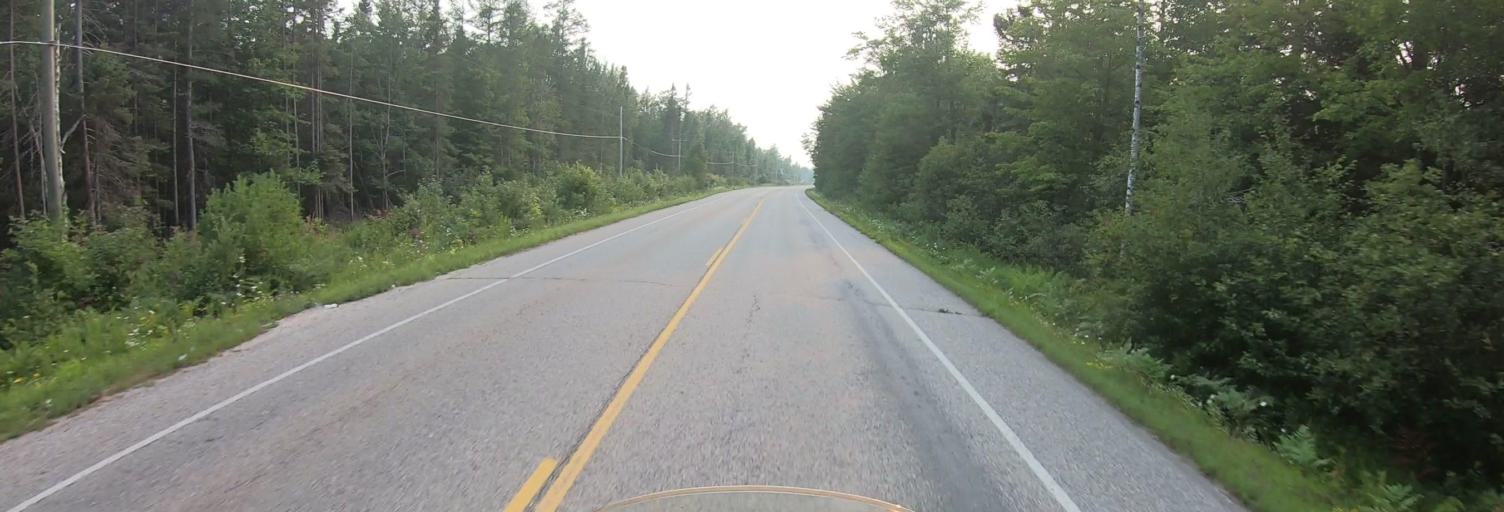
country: US
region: Michigan
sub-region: Chippewa County
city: Sault Ste. Marie
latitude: 46.4145
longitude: -84.5483
